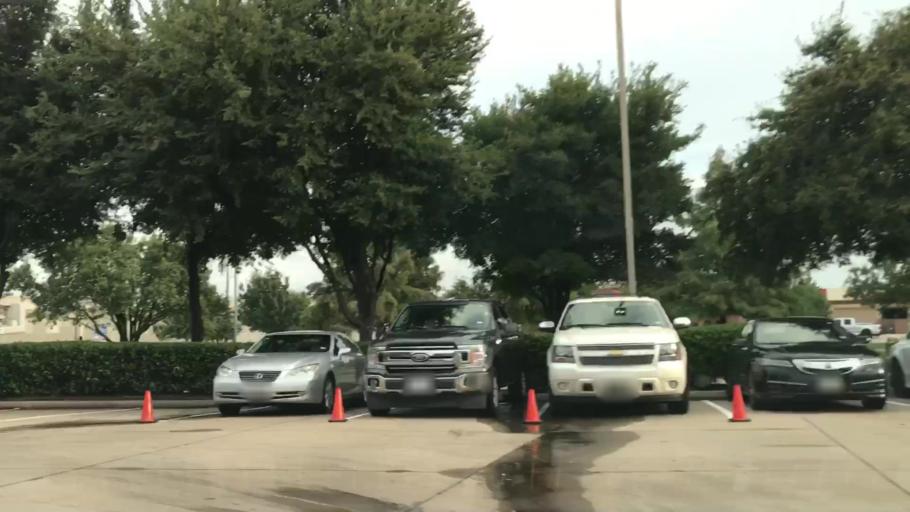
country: US
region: Texas
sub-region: Dallas County
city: Addison
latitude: 33.0281
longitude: -96.8305
